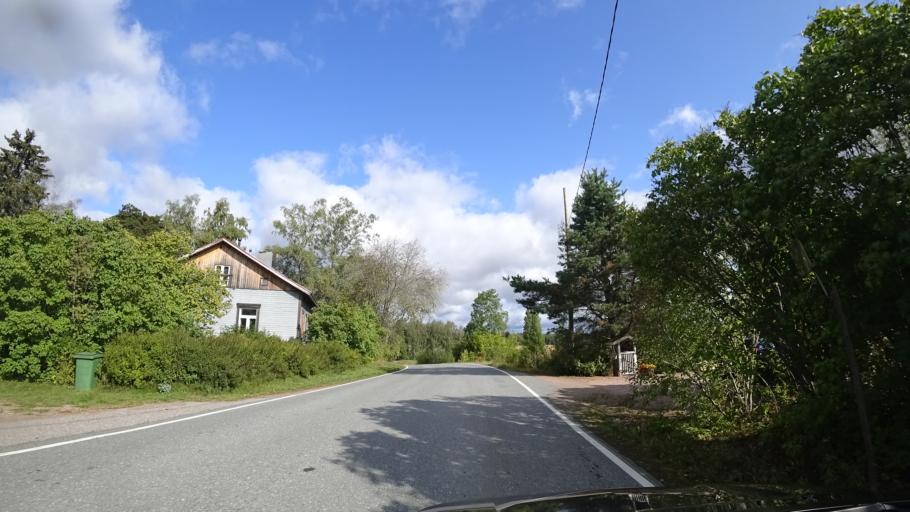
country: FI
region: Haeme
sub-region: Riihimaeki
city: Hausjaervi
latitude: 60.7133
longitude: 24.9718
